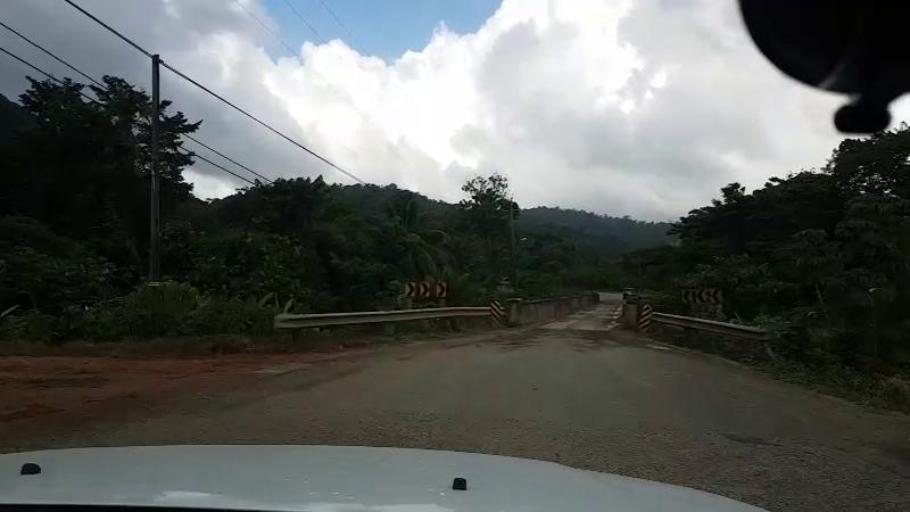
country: BZ
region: Stann Creek
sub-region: Dangriga
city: Dangriga
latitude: 17.0021
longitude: -88.4412
